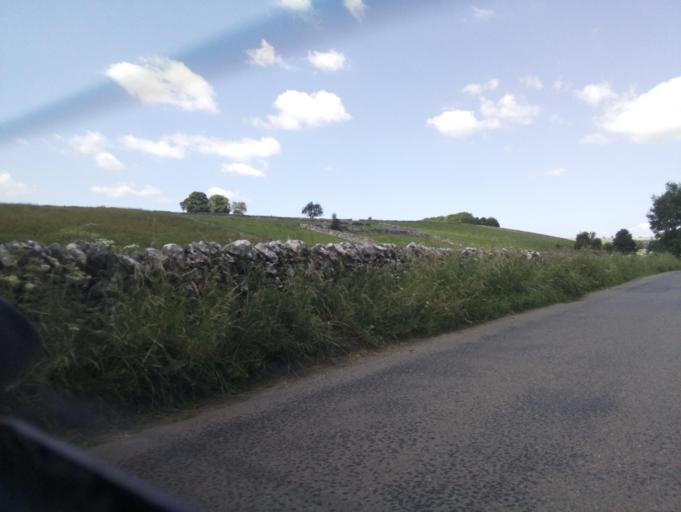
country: GB
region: England
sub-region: Derbyshire
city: Tideswell
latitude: 53.2030
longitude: -1.7775
